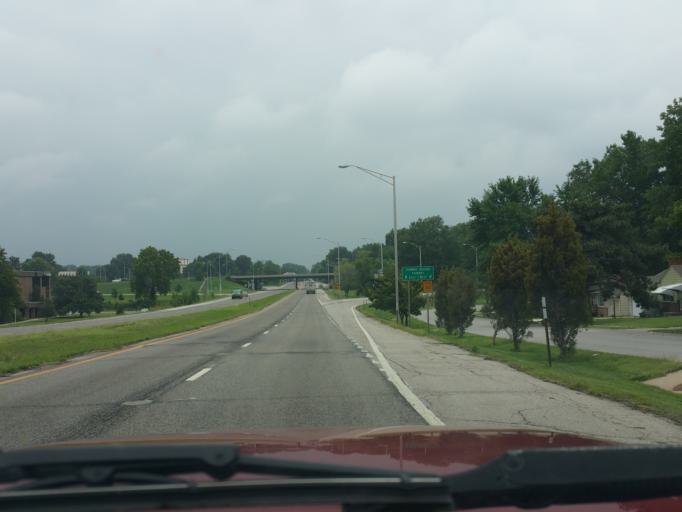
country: US
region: Kansas
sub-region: Johnson County
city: Mission
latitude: 39.0183
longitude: -94.6678
